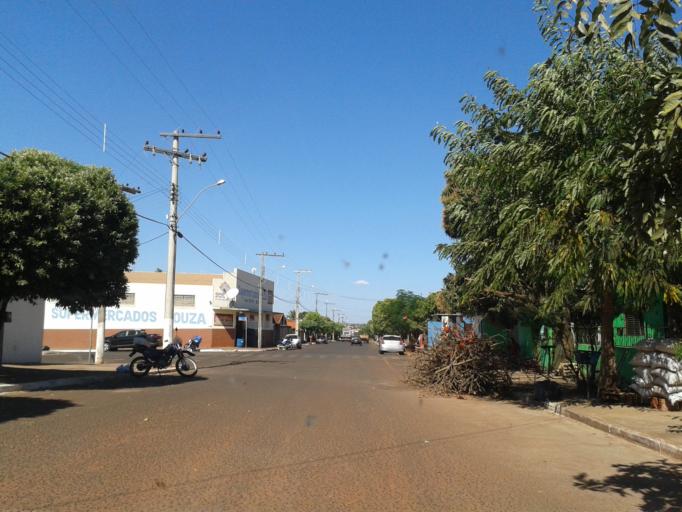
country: BR
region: Minas Gerais
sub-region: Santa Vitoria
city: Santa Vitoria
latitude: -18.8336
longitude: -50.1380
